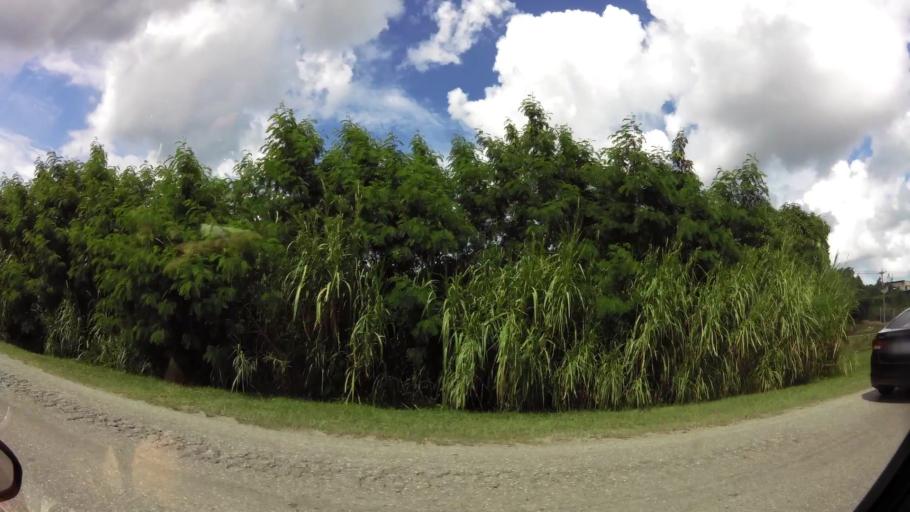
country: TT
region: City of San Fernando
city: San Fernando
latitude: 10.2471
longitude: -61.4950
